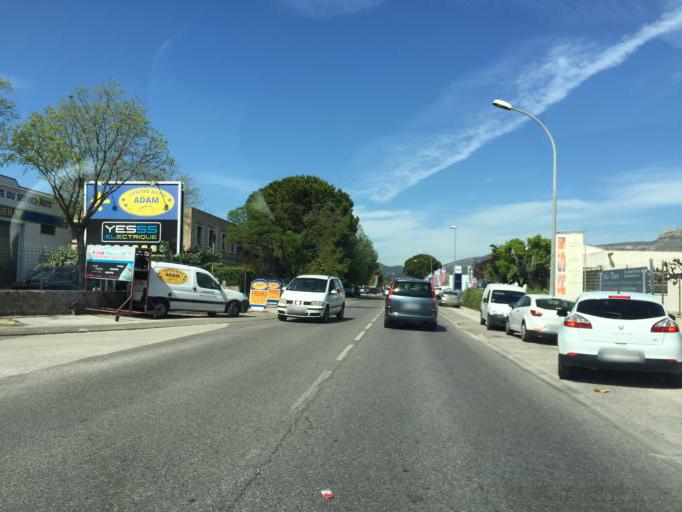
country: FR
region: Provence-Alpes-Cote d'Azur
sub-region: Departement des Bouches-du-Rhone
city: Aubagne
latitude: 43.2900
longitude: 5.5969
